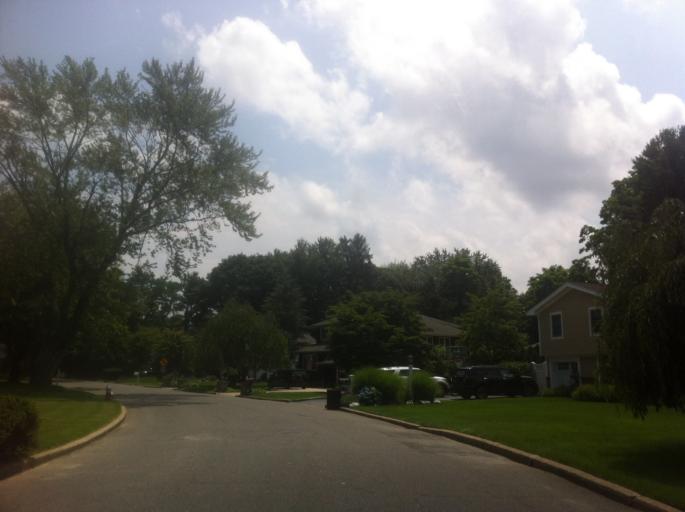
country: US
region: New York
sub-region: Nassau County
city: Locust Valley
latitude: 40.8630
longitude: -73.6015
